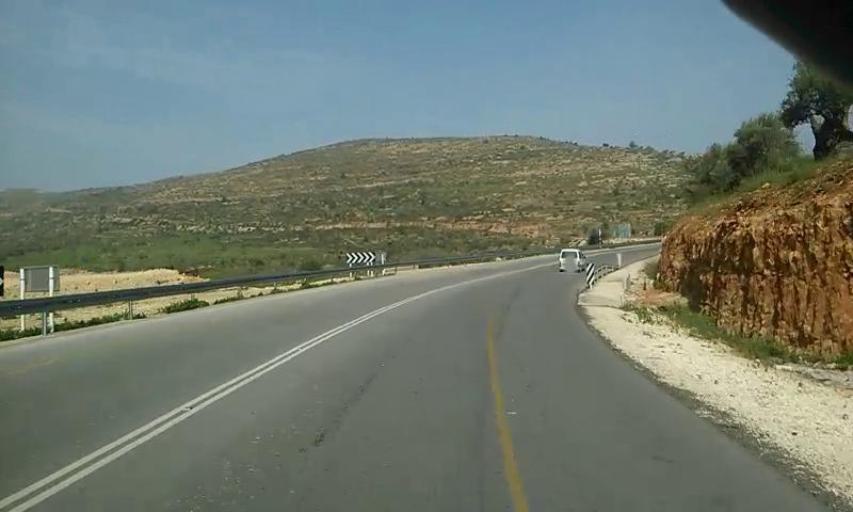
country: PS
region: West Bank
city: `Atarah
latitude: 31.9869
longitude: 35.2277
